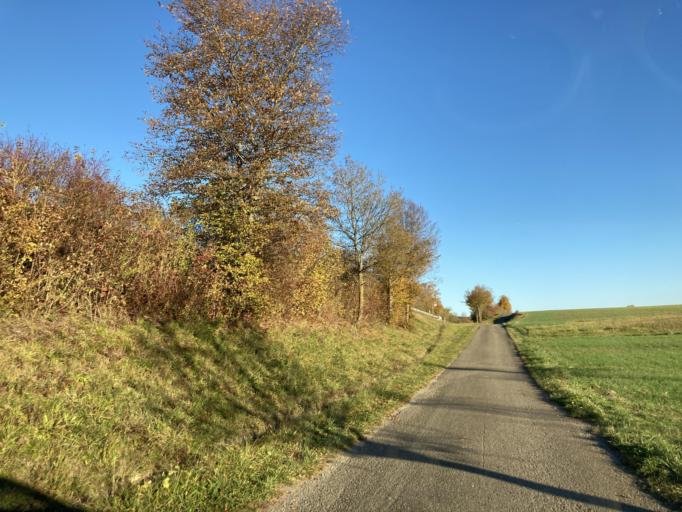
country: DE
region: Baden-Wuerttemberg
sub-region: Tuebingen Region
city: Rottenburg
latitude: 48.4400
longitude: 8.9259
